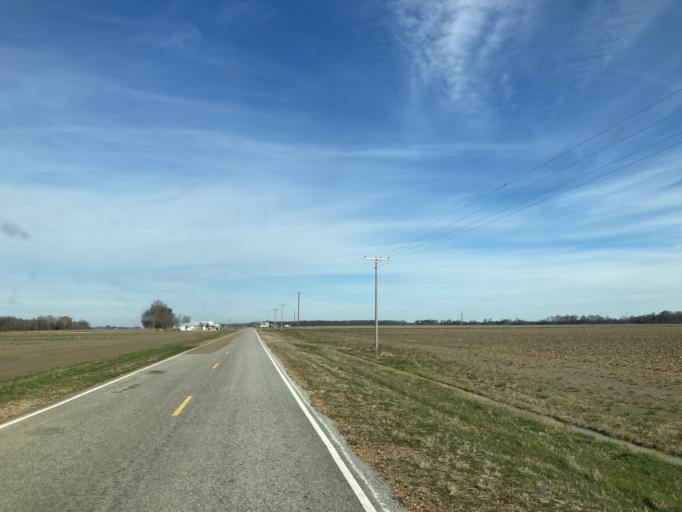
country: US
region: Mississippi
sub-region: Humphreys County
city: Belzoni
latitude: 33.0205
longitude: -90.6230
